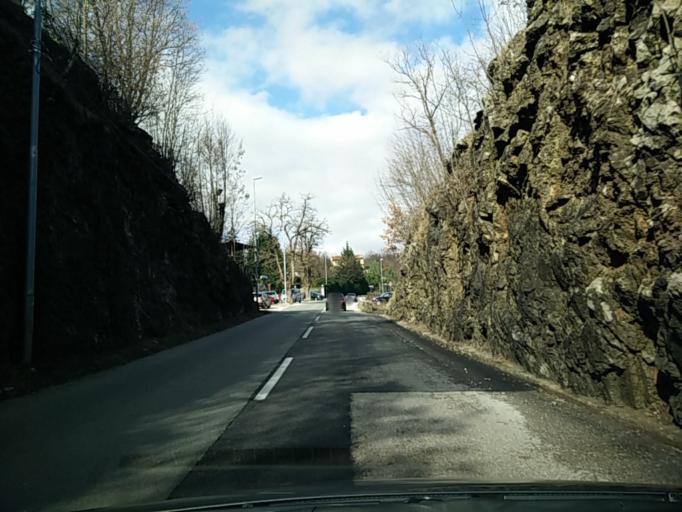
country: HR
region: Primorsko-Goranska
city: Matulji
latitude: 45.3688
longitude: 14.3104
